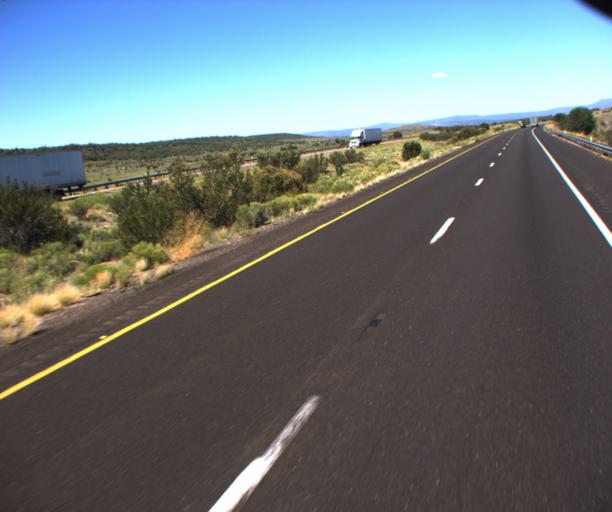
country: US
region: Arizona
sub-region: Yavapai County
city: Paulden
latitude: 35.2728
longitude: -112.7508
